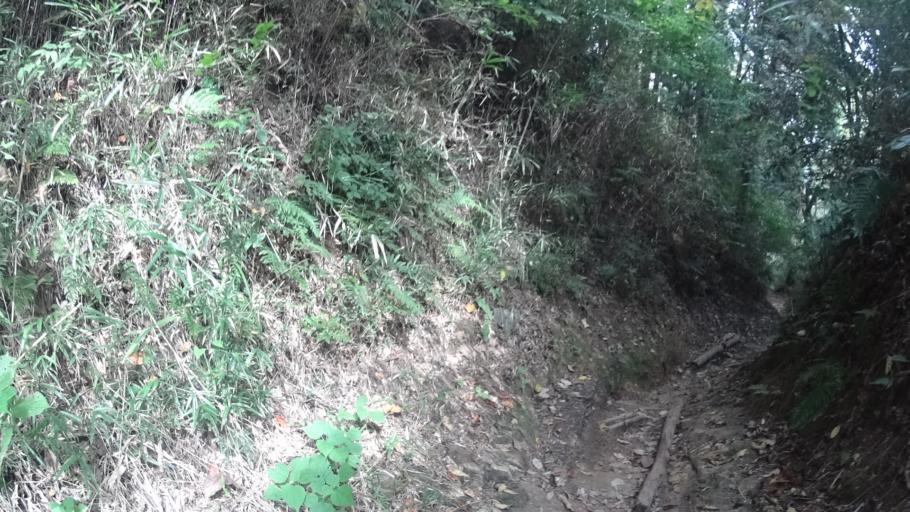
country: JP
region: Kanagawa
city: Zushi
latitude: 35.2945
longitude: 139.6019
